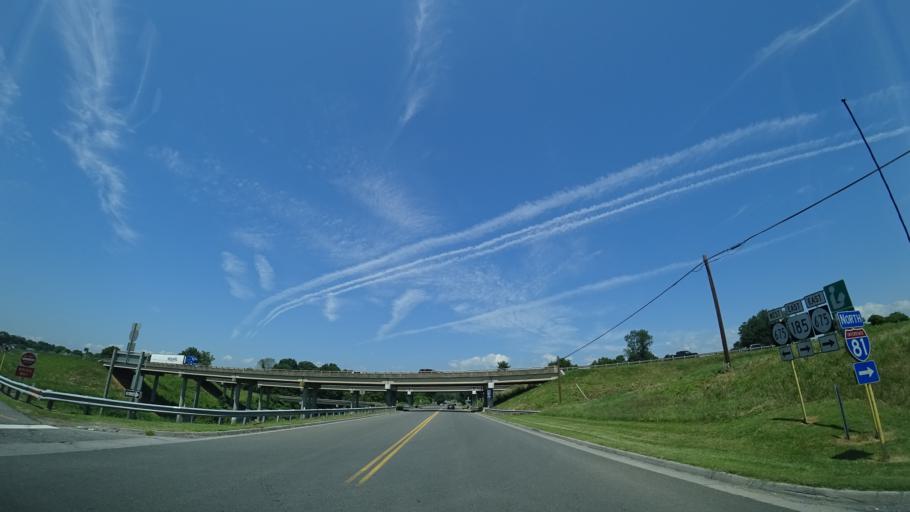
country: US
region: Virginia
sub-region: Shenandoah County
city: Edinburg
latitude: 38.8297
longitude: -78.5754
